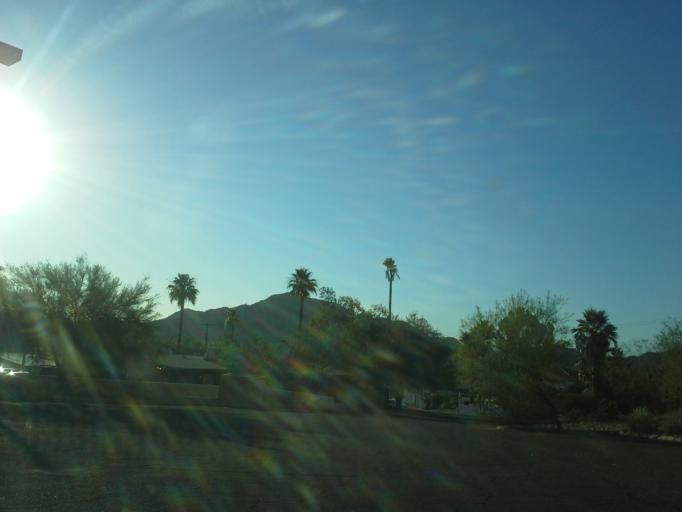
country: US
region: Arizona
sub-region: Maricopa County
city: Paradise Valley
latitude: 33.5670
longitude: -112.0510
